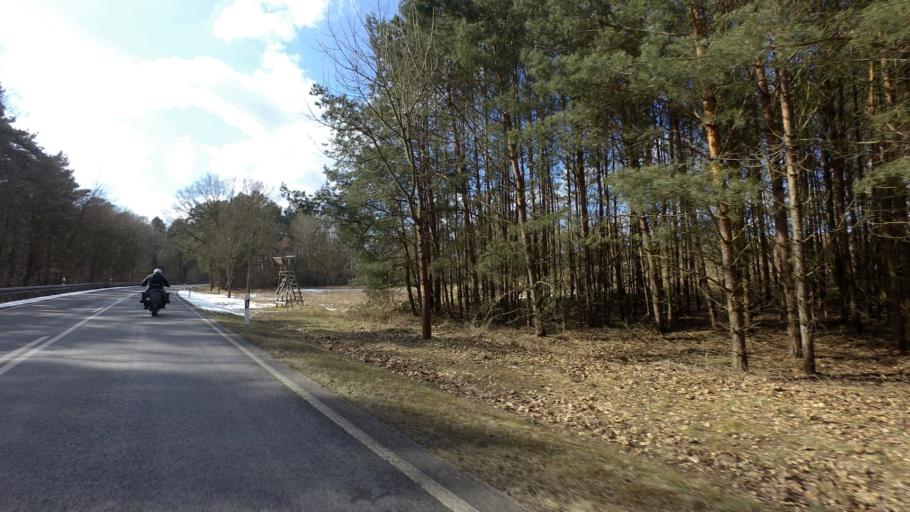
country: DE
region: Brandenburg
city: Marienwerder
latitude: 52.8507
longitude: 13.5889
